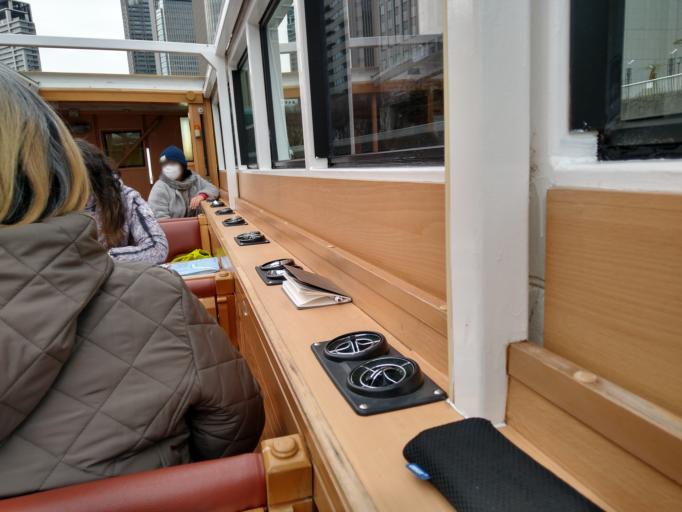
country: JP
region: Osaka
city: Osaka-shi
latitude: 34.6931
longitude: 135.4994
